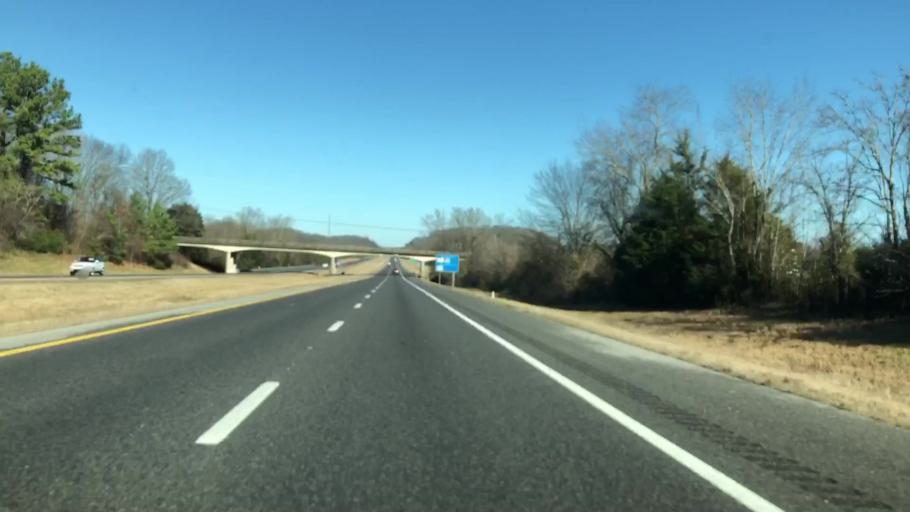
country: US
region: Alabama
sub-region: Limestone County
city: Ardmore
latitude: 35.0606
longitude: -86.8813
